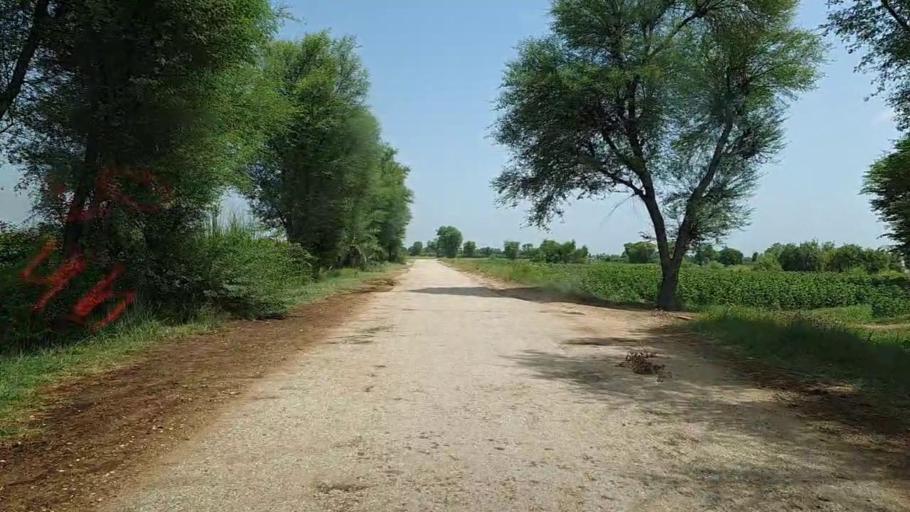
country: PK
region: Sindh
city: Bhiria
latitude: 26.8932
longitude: 68.1978
